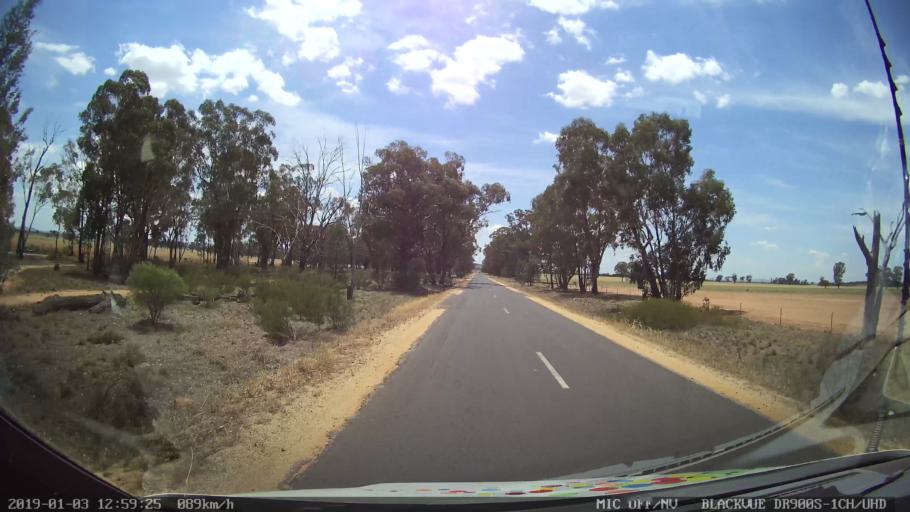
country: AU
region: New South Wales
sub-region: Cabonne
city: Canowindra
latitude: -33.6370
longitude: 148.3890
